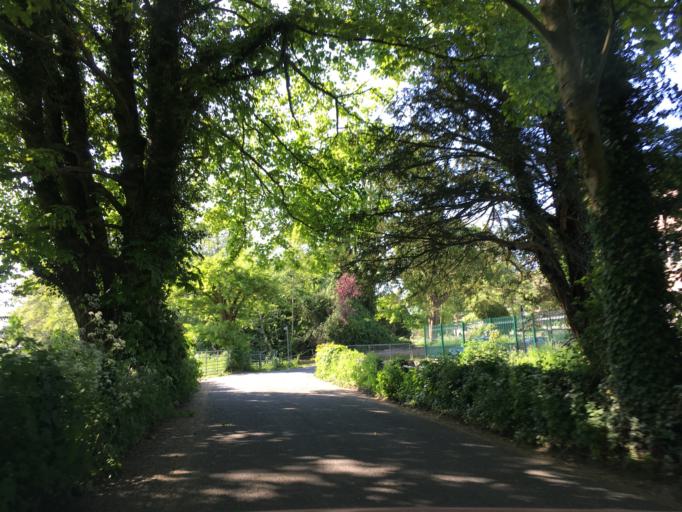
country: GB
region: England
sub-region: Gloucestershire
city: Stonehouse
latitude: 51.7495
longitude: -2.3155
